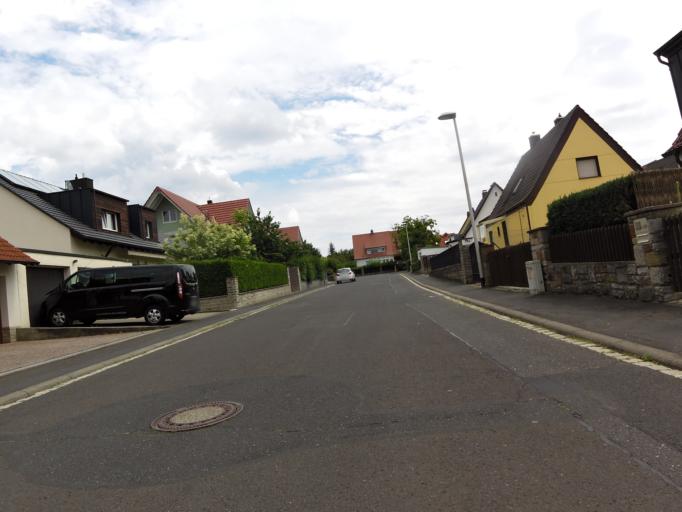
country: DE
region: Bavaria
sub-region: Regierungsbezirk Unterfranken
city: Eibelstadt
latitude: 49.7236
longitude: 9.9693
